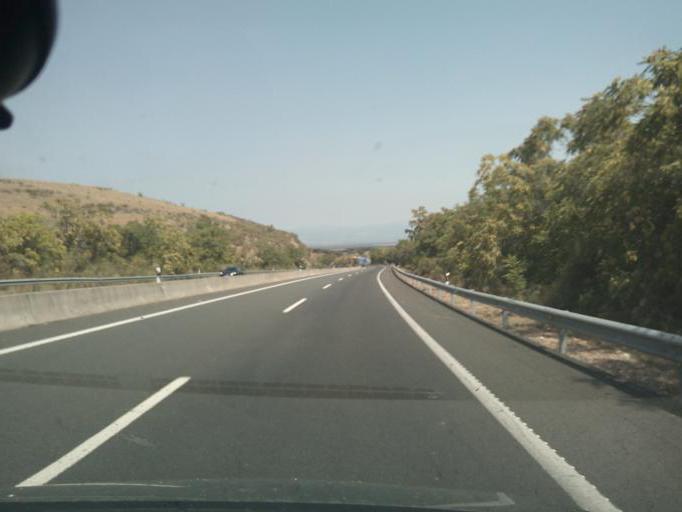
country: ES
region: Extremadura
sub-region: Provincia de Caceres
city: Romangordo
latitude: 39.7480
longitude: -5.7267
